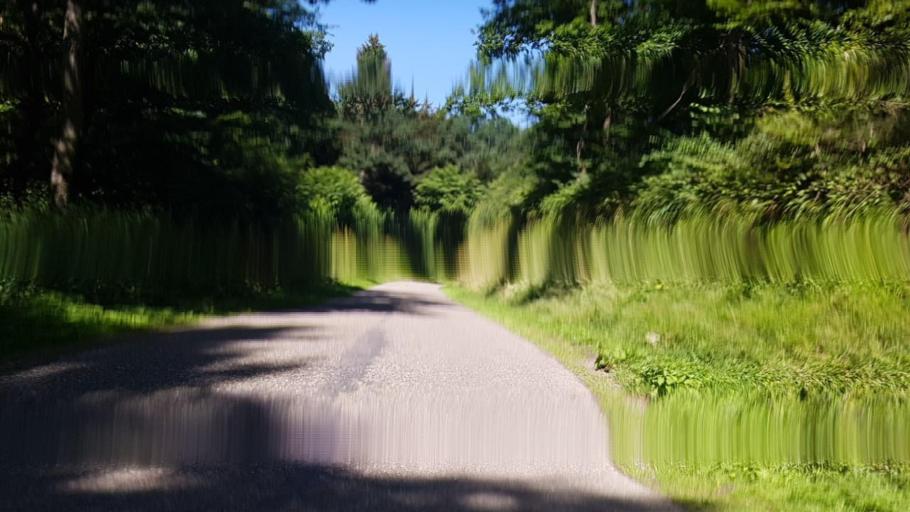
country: BE
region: Wallonia
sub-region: Province du Hainaut
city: Froidchapelle
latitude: 50.1249
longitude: 4.2481
